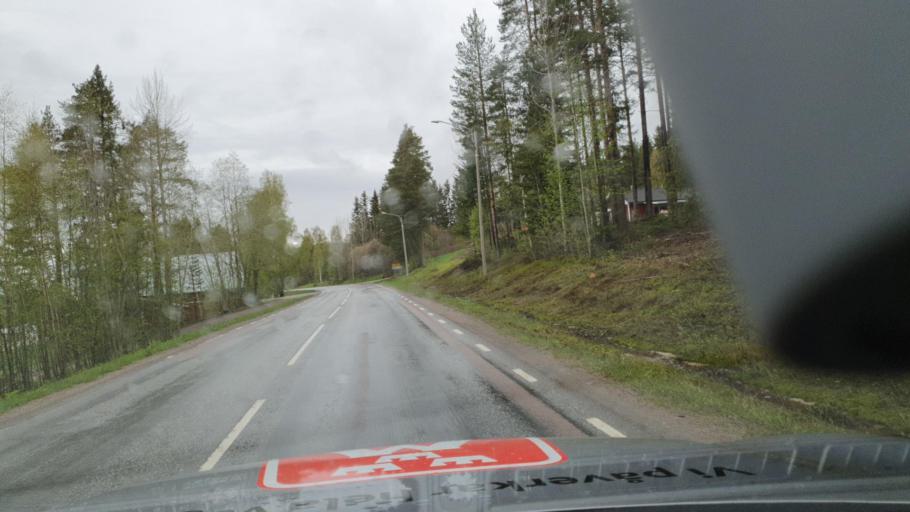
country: SE
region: Vaesternorrland
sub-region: OErnskoeldsviks Kommun
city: Bjasta
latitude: 63.3498
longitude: 18.5280
